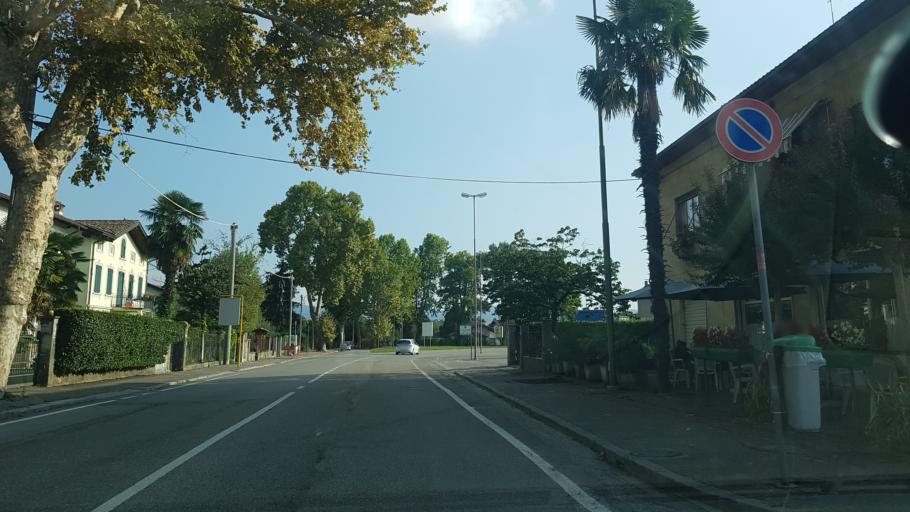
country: IT
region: Friuli Venezia Giulia
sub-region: Provincia di Gorizia
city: Gorizia
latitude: 45.9412
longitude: 13.6351
